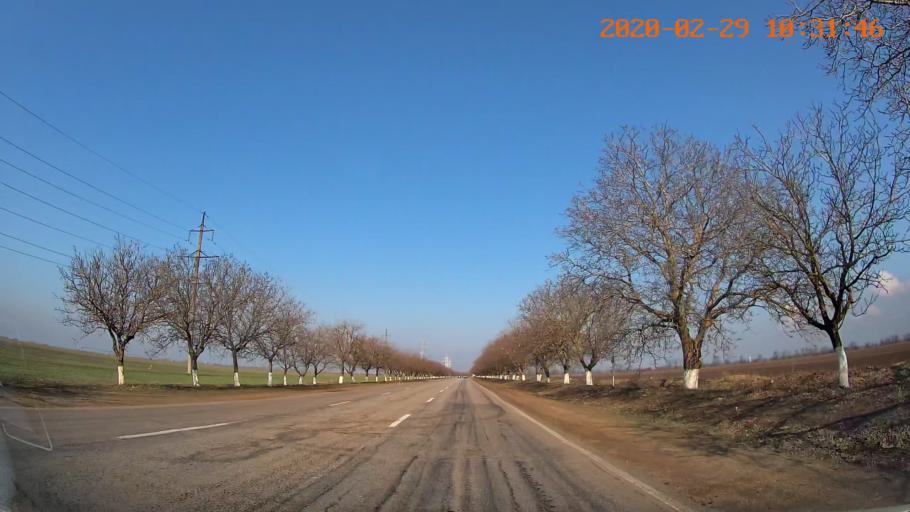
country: UA
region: Odessa
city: Velykoploske
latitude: 46.9527
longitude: 29.5602
